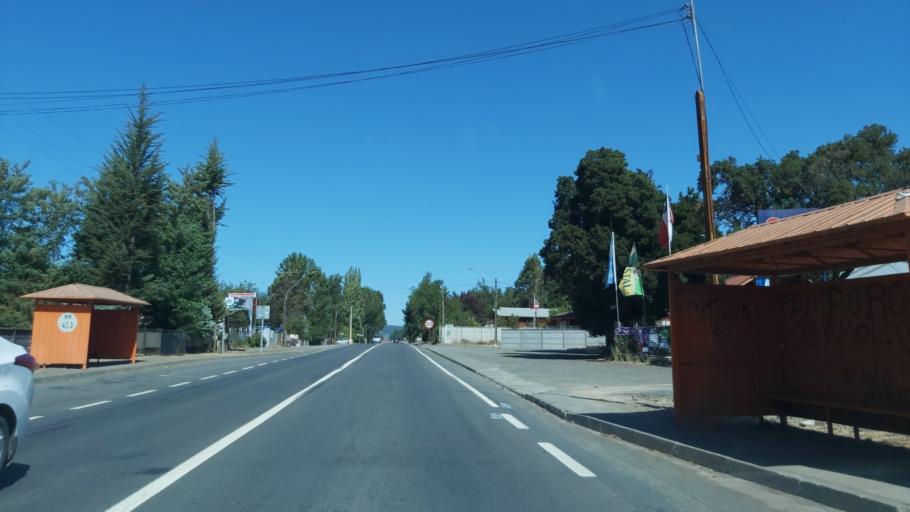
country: CL
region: Biobio
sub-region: Provincia de Concepcion
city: Lota
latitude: -37.1527
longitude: -72.9748
